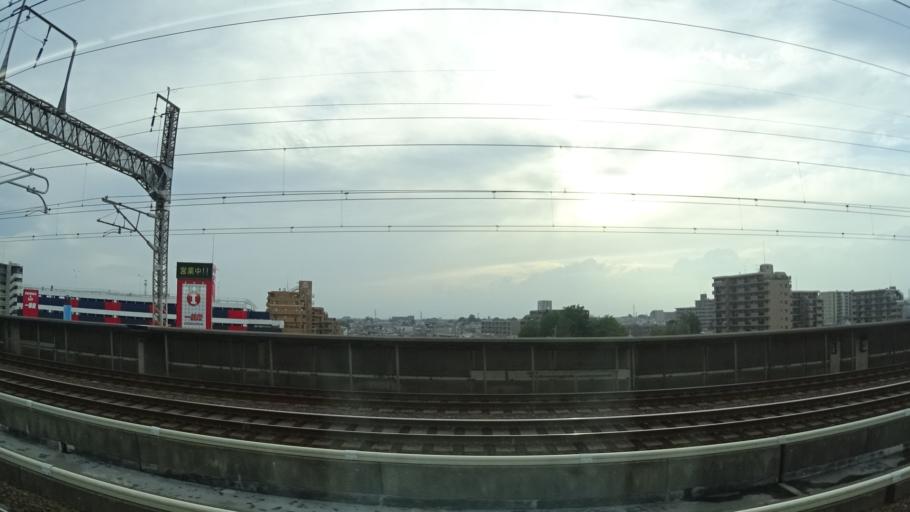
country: JP
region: Saitama
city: Ageoshimo
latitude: 35.9290
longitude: 139.6163
